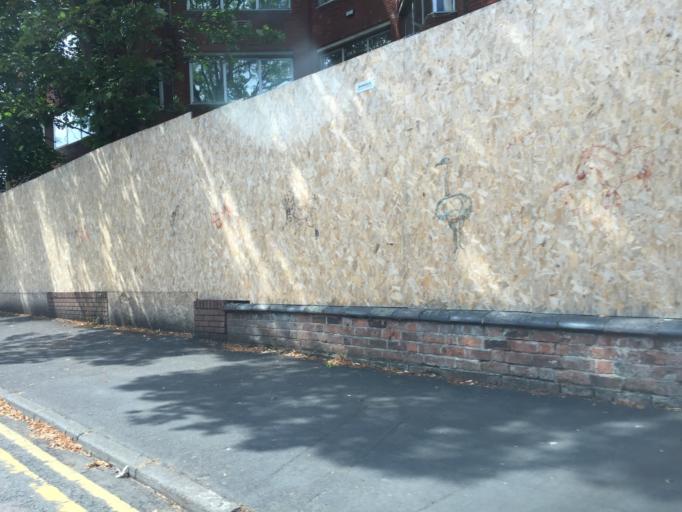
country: GB
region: England
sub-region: Gloucestershire
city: Gloucester
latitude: 51.8687
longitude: -2.2347
